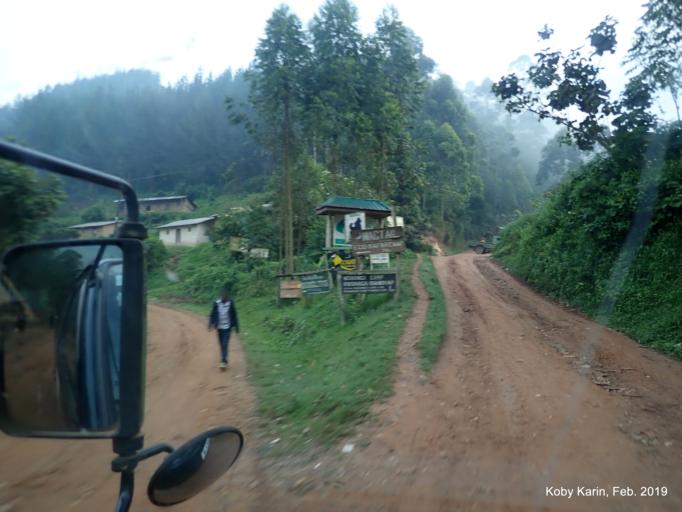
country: UG
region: Western Region
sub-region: Kisoro District
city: Kisoro
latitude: -1.1280
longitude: 29.7137
